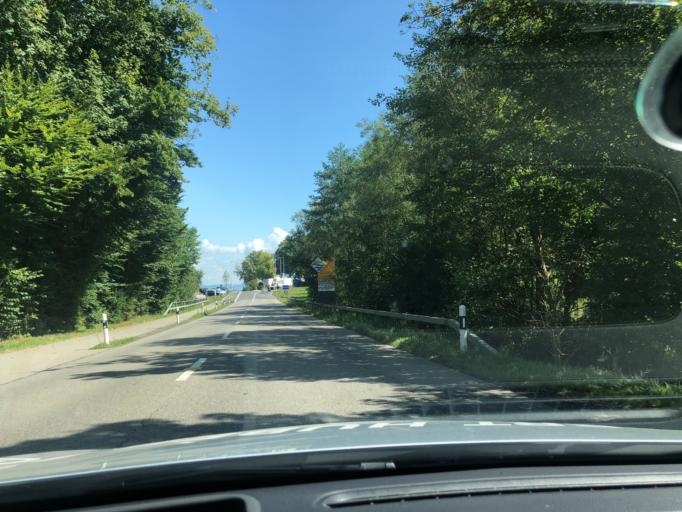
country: CH
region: Thurgau
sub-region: Kreuzlingen District
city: Tagerwilen
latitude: 47.6354
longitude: 9.1542
